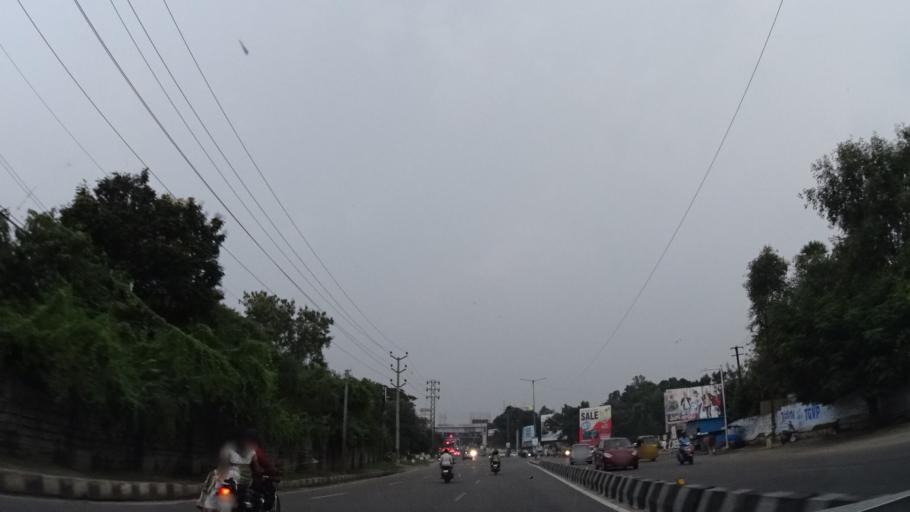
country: IN
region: Telangana
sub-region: Hyderabad
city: Malkajgiri
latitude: 17.4463
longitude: 78.4874
